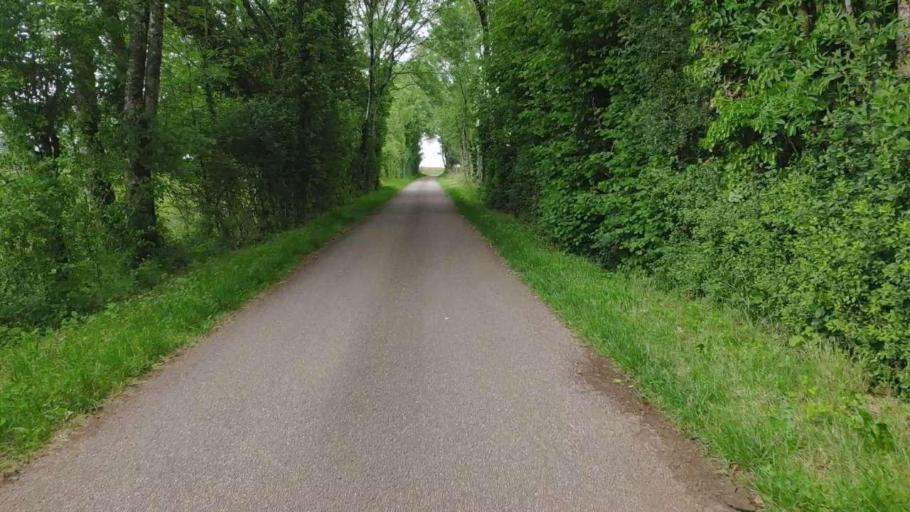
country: FR
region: Franche-Comte
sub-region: Departement du Jura
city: Poligny
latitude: 46.7622
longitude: 5.6401
